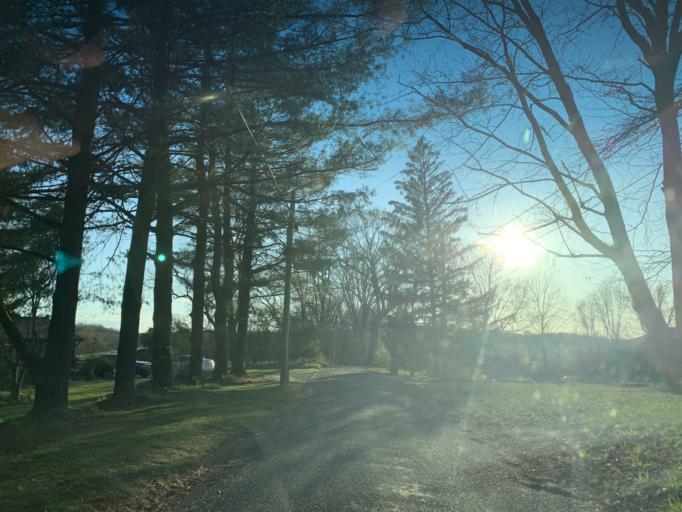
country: US
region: Maryland
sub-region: Harford County
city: South Bel Air
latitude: 39.5757
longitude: -76.2622
